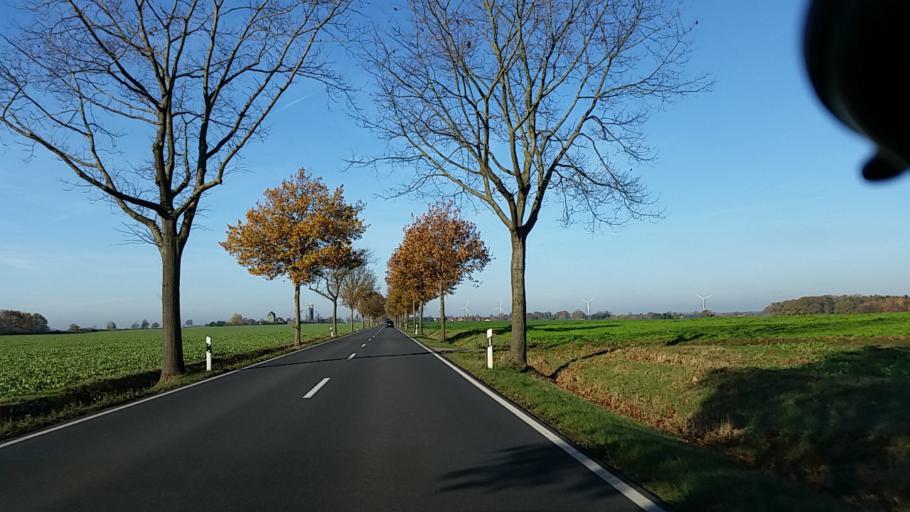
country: DE
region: Saxony-Anhalt
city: Jubar
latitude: 52.6862
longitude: 10.8226
